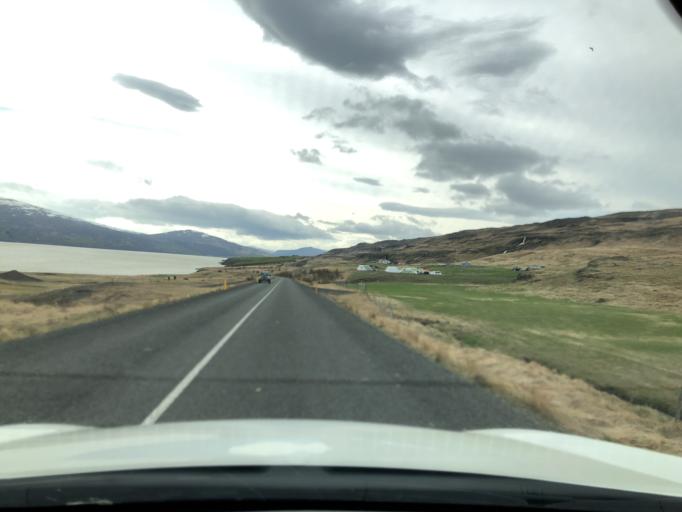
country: IS
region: East
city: Egilsstadir
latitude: 65.1322
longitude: -14.7556
